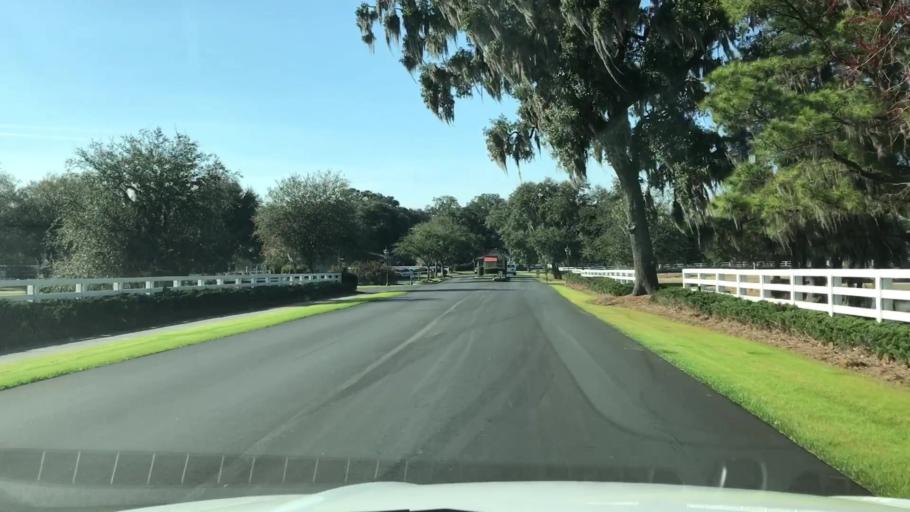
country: US
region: South Carolina
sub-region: Beaufort County
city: Bluffton
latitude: 32.3455
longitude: -80.9239
